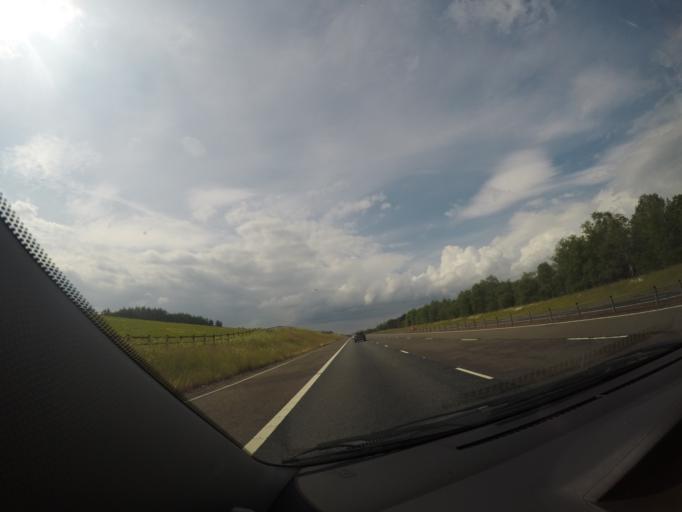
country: GB
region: Scotland
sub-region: Dumfries and Galloway
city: Lockerbie
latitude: 55.1678
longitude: -3.3908
